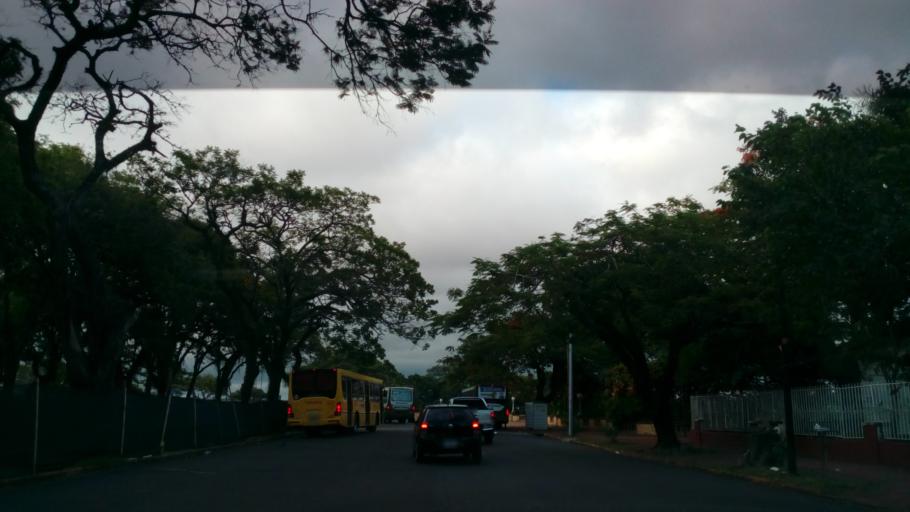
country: AR
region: Misiones
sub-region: Departamento de Capital
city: Posadas
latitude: -27.3554
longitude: -55.8932
